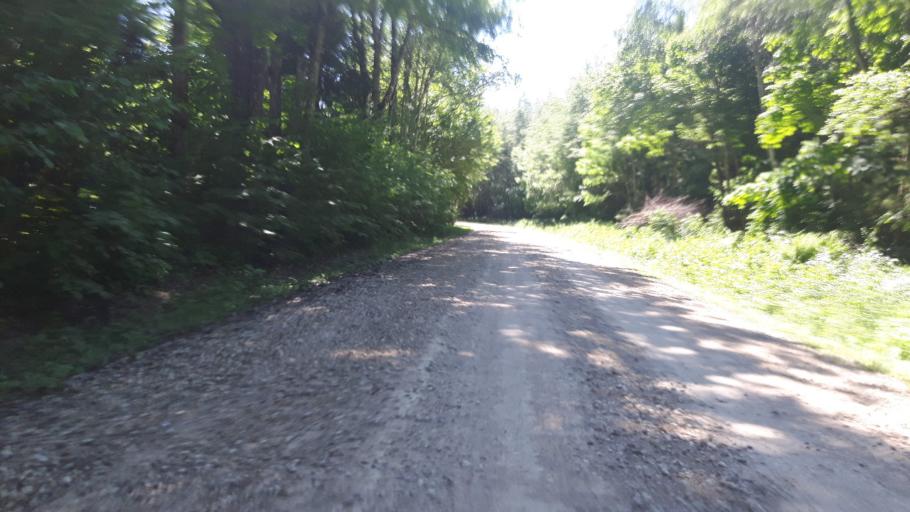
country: EE
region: Paernumaa
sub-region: Tootsi vald
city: Tootsi
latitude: 58.5055
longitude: 24.9061
